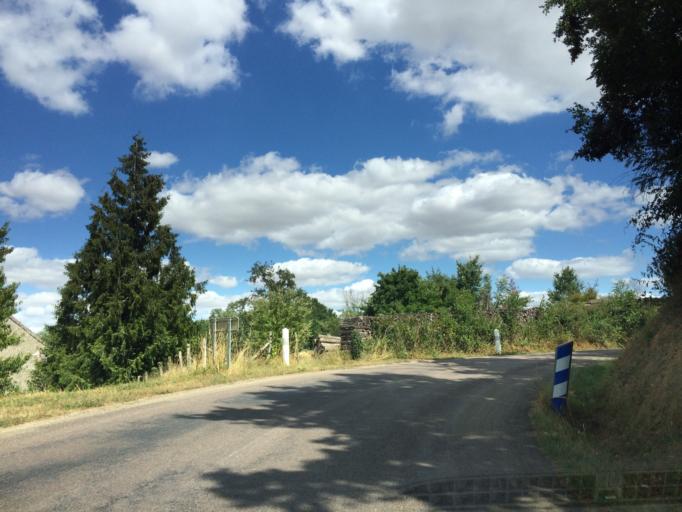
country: FR
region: Bourgogne
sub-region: Departement de l'Yonne
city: Fleury-la-Vallee
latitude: 47.8687
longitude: 3.4064
